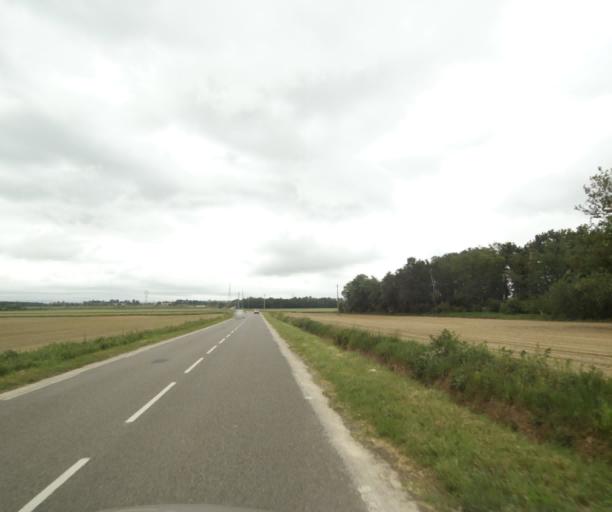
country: FR
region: Rhone-Alpes
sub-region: Departement de l'Ain
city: Saint-Maurice-de-Beynost
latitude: 45.8508
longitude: 4.9584
